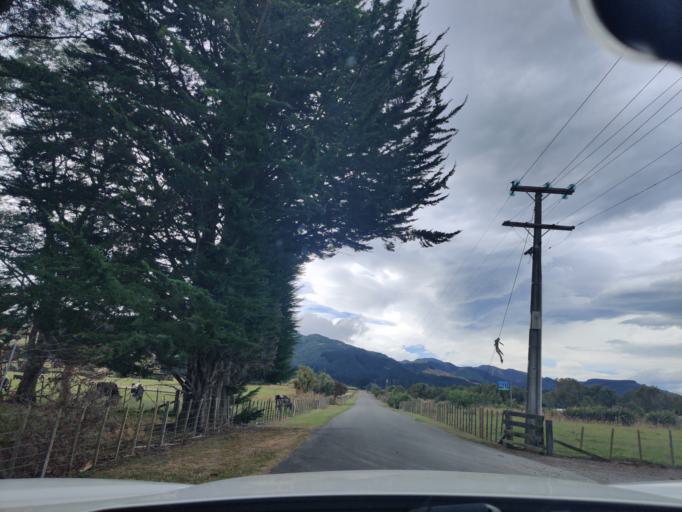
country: NZ
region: Wellington
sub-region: Masterton District
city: Masterton
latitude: -41.0361
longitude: 175.4460
